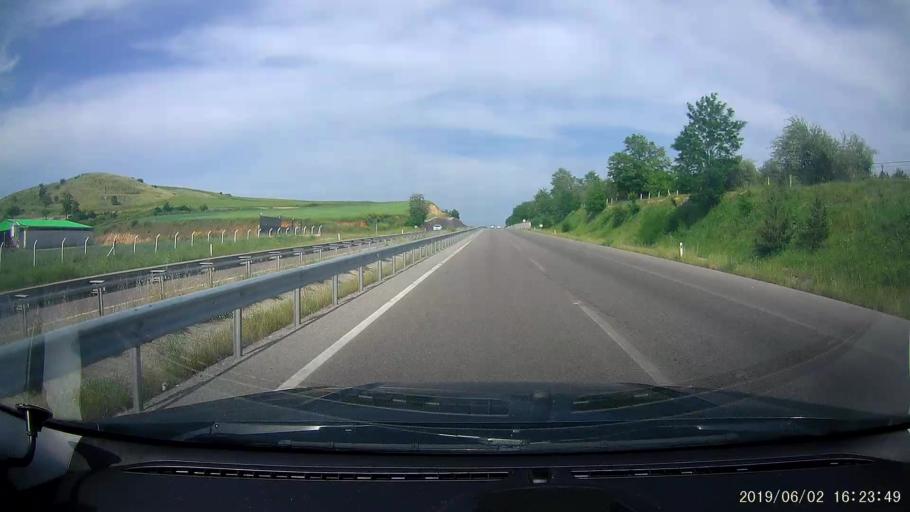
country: TR
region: Samsun
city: Havza
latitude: 40.9958
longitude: 35.7439
